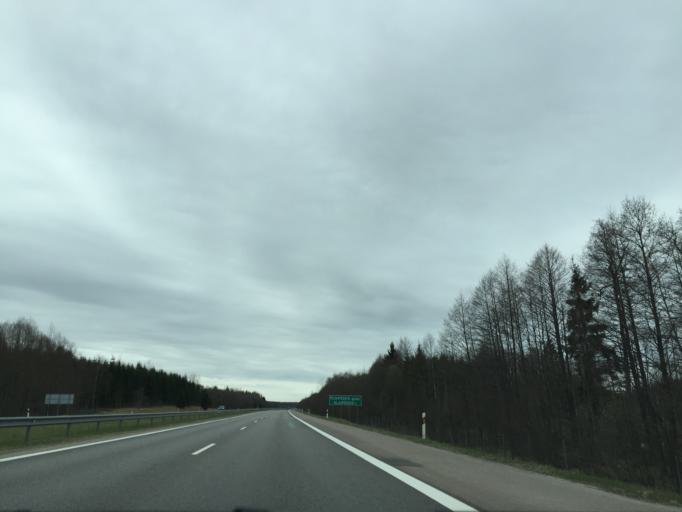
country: LT
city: Rietavas
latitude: 55.6523
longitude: 21.7927
